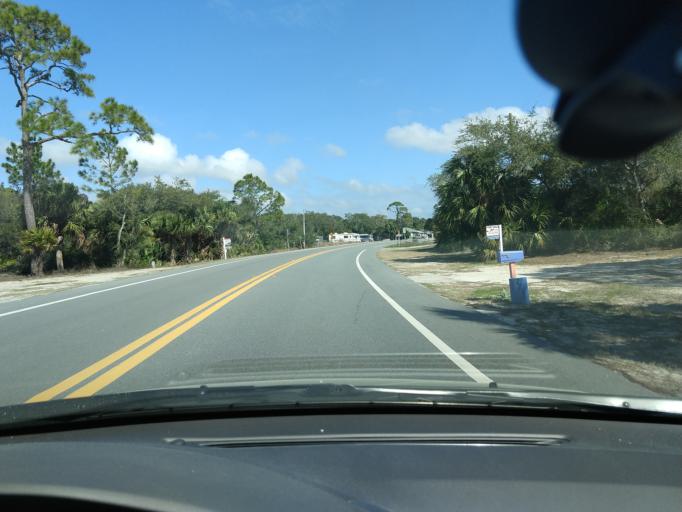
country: US
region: Florida
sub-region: Gulf County
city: Port Saint Joe
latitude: 29.6828
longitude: -85.2248
